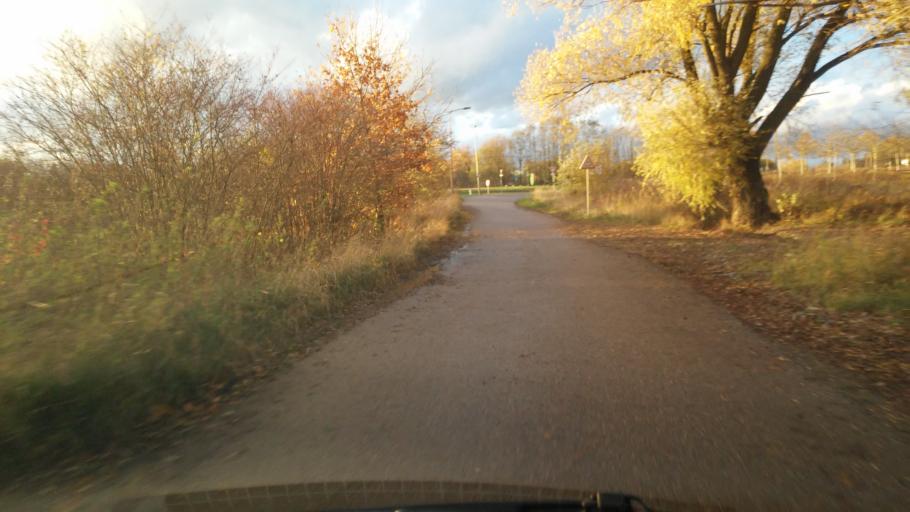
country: FR
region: Lorraine
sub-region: Departement de la Moselle
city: Talange
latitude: 49.2369
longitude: 6.1848
